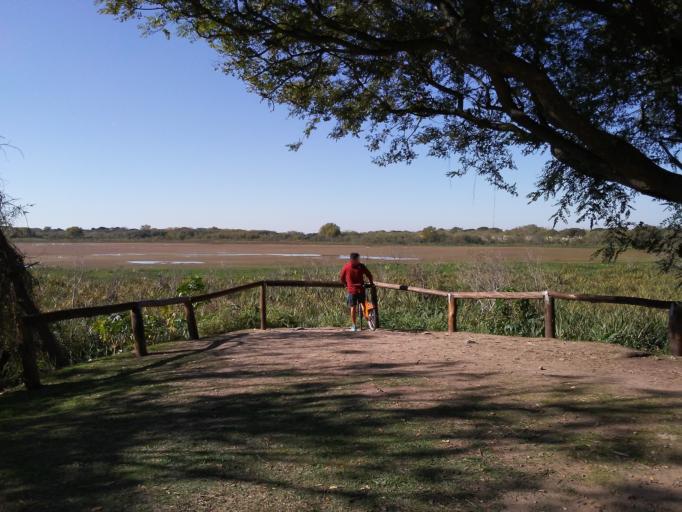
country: AR
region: Buenos Aires F.D.
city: Buenos Aires
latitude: -34.6074
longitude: -58.3579
